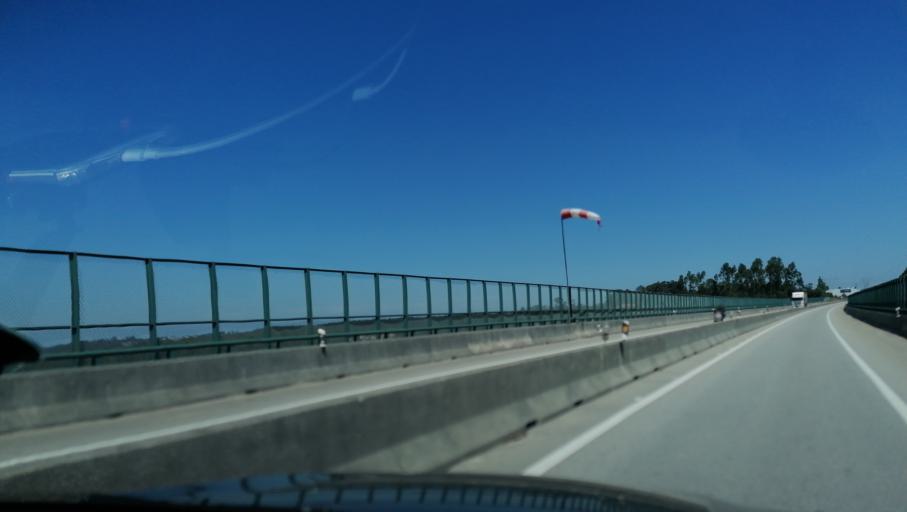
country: PT
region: Aveiro
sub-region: Agueda
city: Agueda
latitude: 40.5719
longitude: -8.4756
